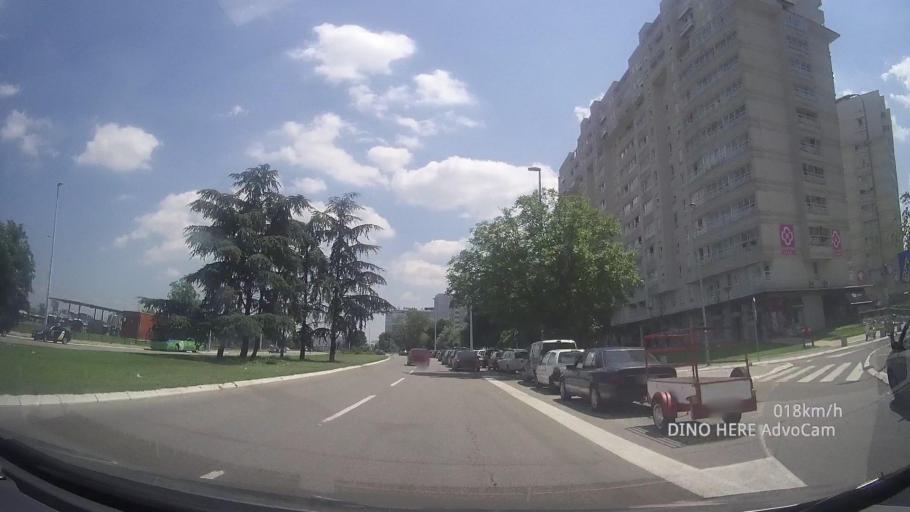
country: RS
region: Central Serbia
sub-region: Belgrade
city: Novi Beograd
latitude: 44.8071
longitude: 20.4065
